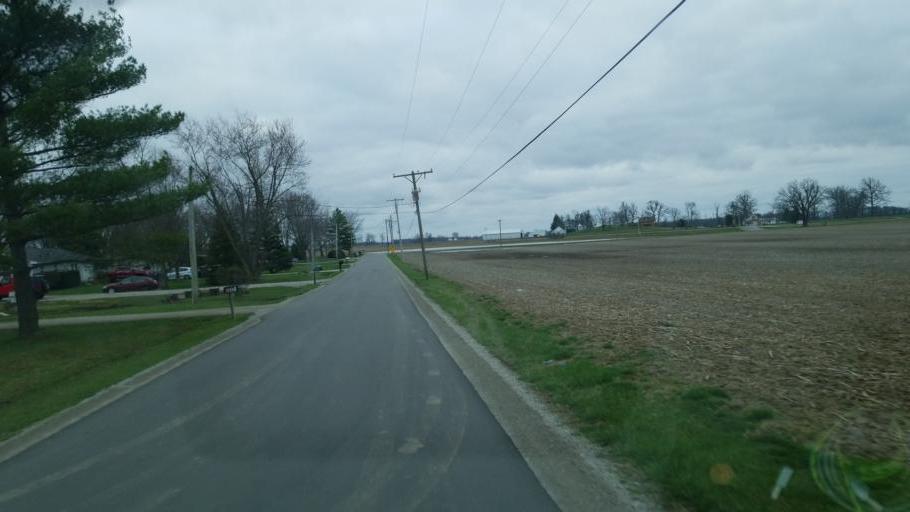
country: US
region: Ohio
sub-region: Fayette County
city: Jeffersonville
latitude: 39.5903
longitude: -83.5133
